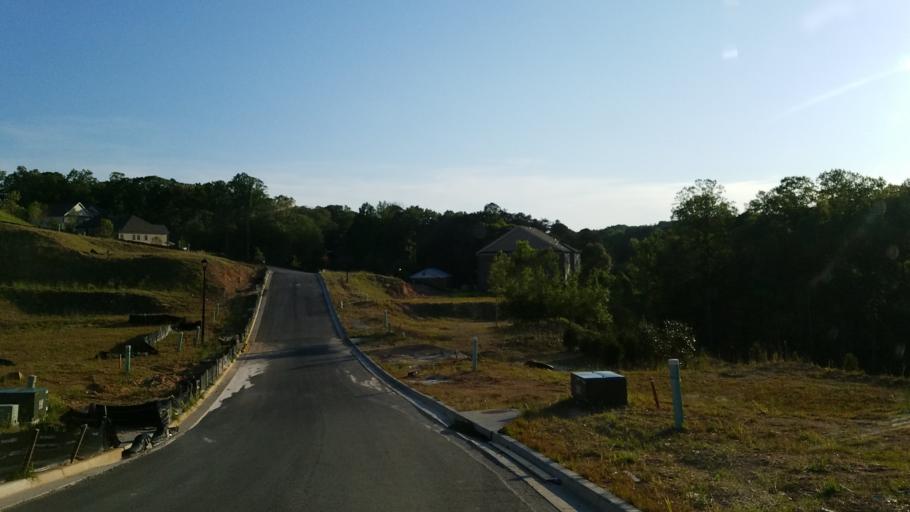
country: US
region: Georgia
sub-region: Cobb County
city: Vinings
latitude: 33.8716
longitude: -84.4819
